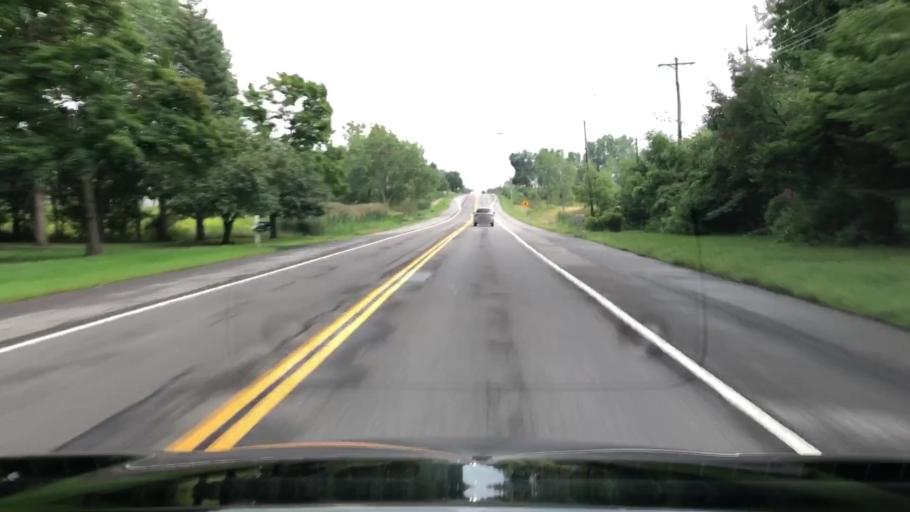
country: US
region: New York
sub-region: Erie County
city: Orchard Park
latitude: 42.8089
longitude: -78.6970
